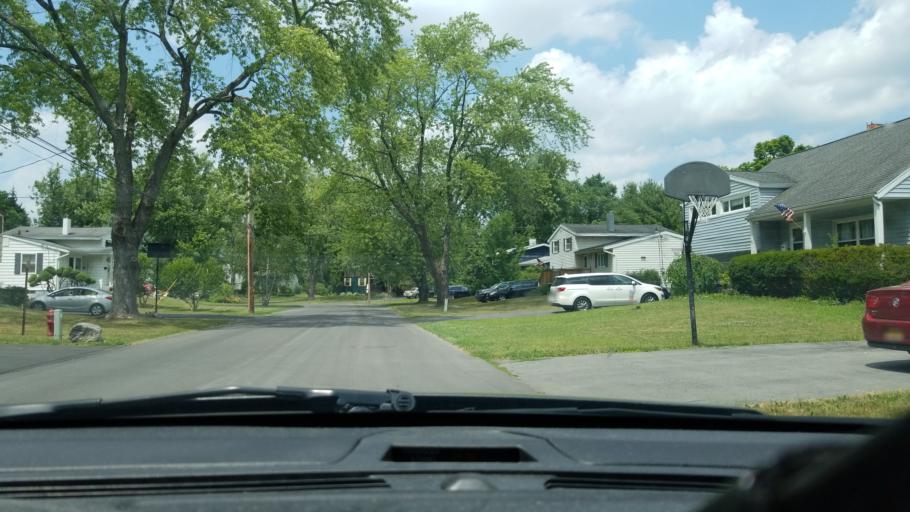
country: US
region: New York
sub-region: Onondaga County
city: Liverpool
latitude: 43.1399
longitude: -76.2139
